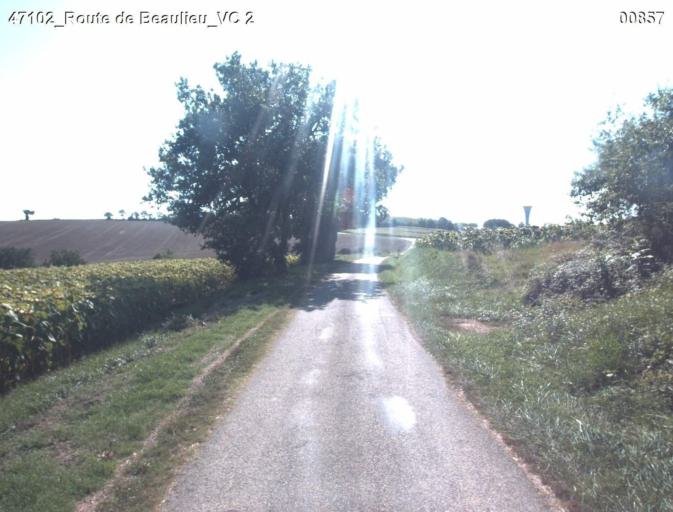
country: FR
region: Aquitaine
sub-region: Departement du Lot-et-Garonne
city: Laplume
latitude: 44.0811
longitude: 0.4395
